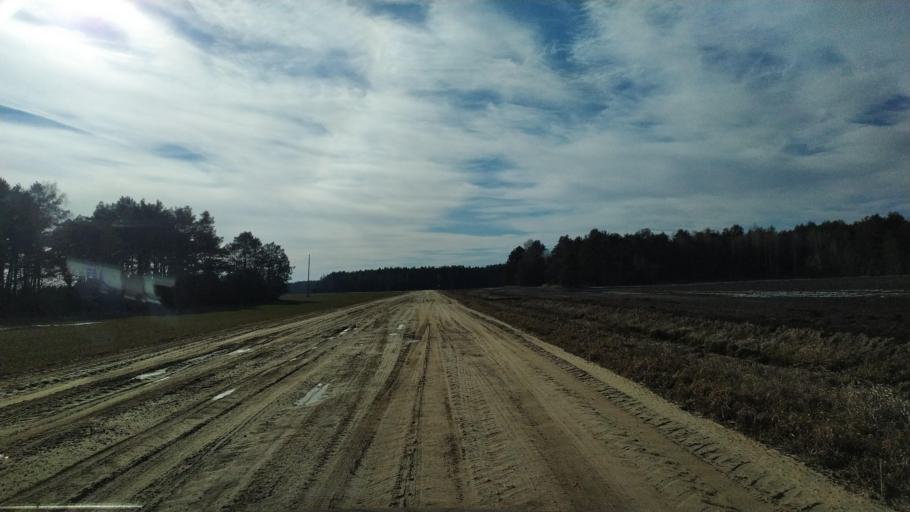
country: BY
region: Brest
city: Pruzhany
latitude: 52.5738
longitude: 24.3013
